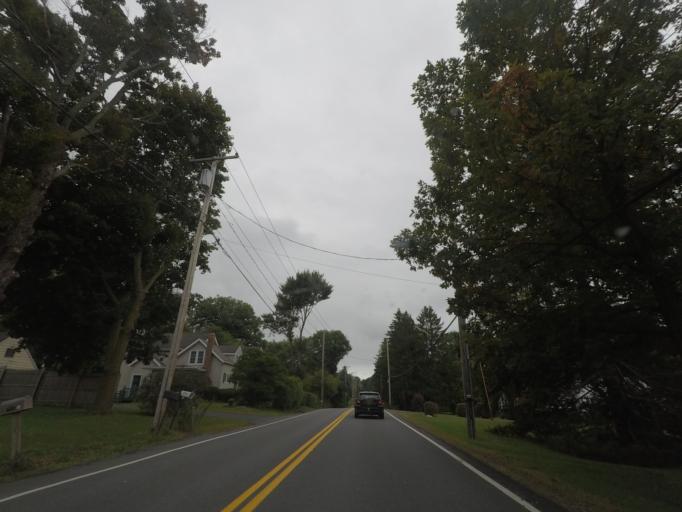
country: US
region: New York
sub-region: Rensselaer County
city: Hampton Manor
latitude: 42.6491
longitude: -73.6887
